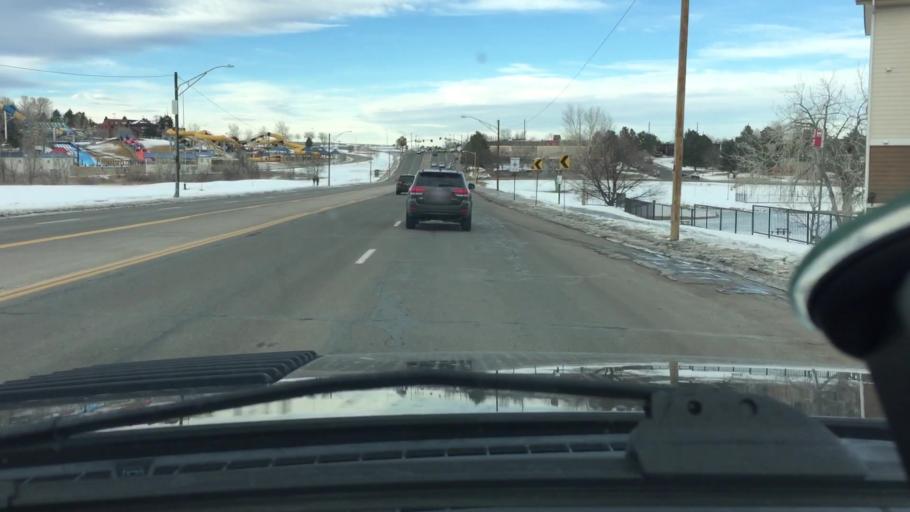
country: US
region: Colorado
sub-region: Adams County
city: Federal Heights
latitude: 39.8523
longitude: -105.0060
